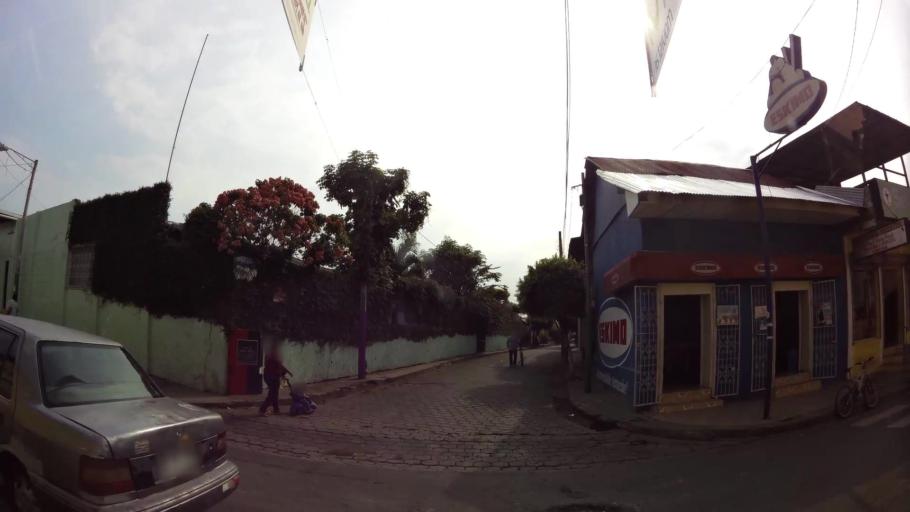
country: NI
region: Masaya
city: Masaya
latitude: 11.9683
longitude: -86.0941
